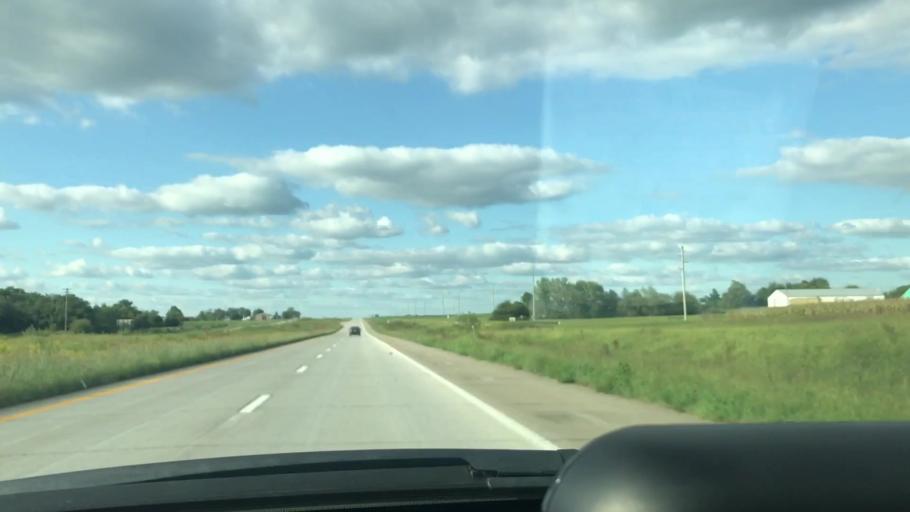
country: US
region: Missouri
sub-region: Benton County
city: Cole Camp
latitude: 38.4937
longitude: -93.2735
